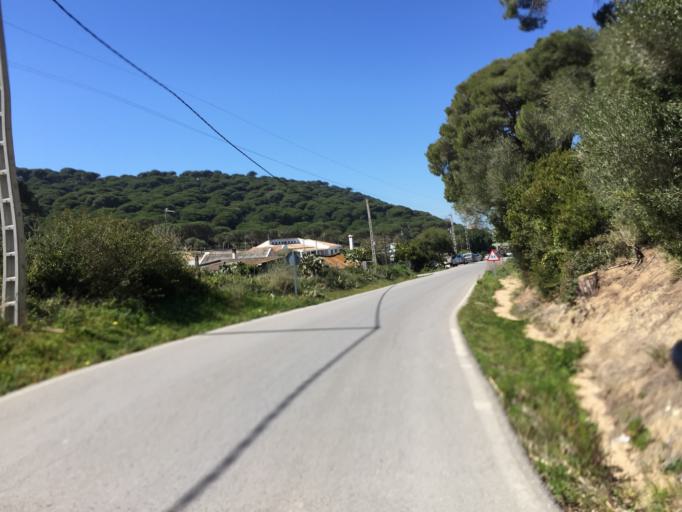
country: ES
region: Andalusia
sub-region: Provincia de Cadiz
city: Vejer de la Frontera
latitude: 36.2052
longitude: -5.9913
